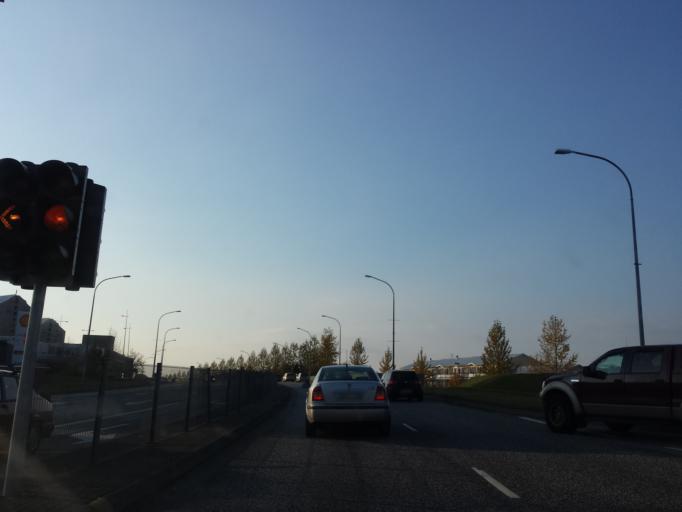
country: IS
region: Capital Region
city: Kopavogur
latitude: 64.1026
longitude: -21.8830
